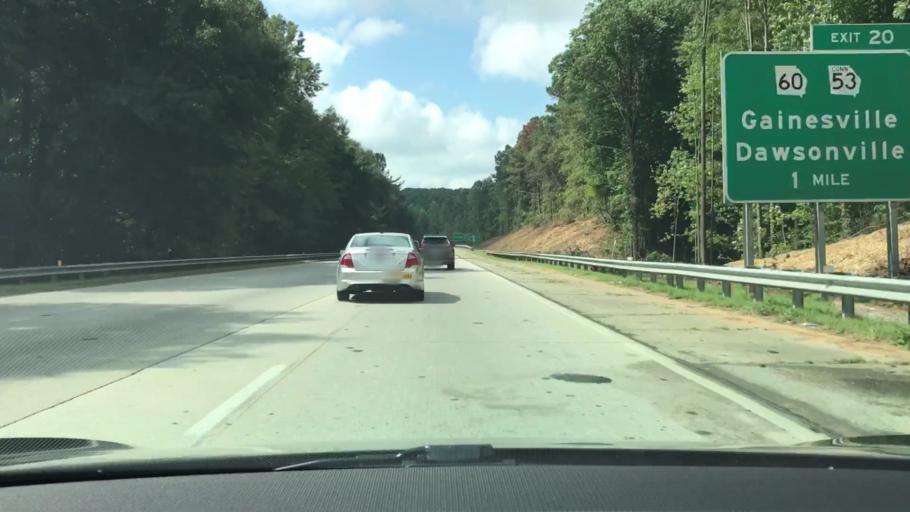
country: US
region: Georgia
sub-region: Hall County
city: Gainesville
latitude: 34.2790
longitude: -83.8107
